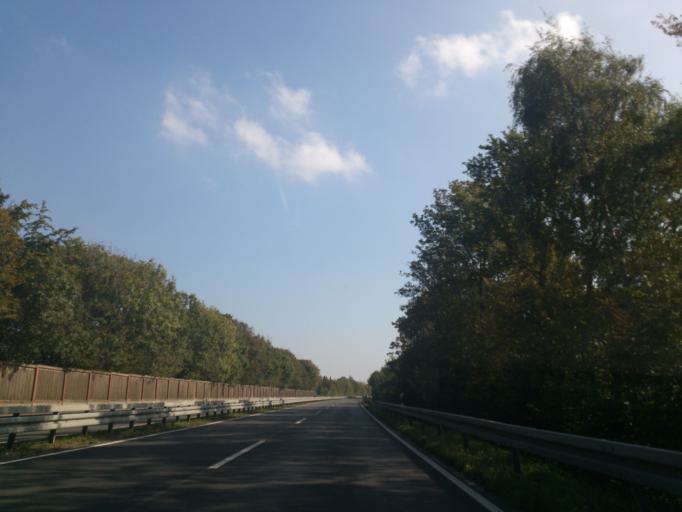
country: DE
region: North Rhine-Westphalia
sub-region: Regierungsbezirk Detmold
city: Paderborn
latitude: 51.7013
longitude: 8.7468
